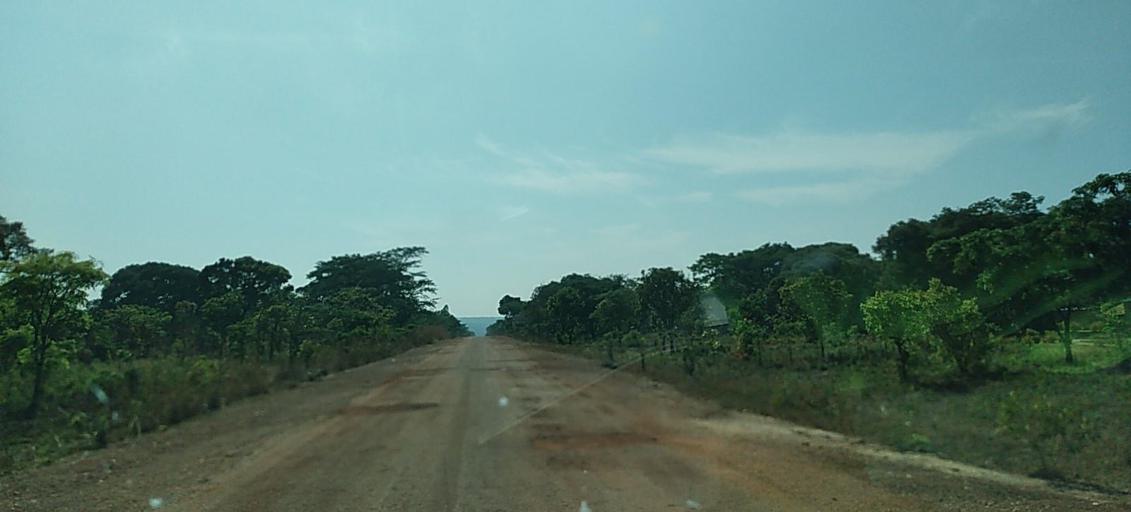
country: ZM
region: North-Western
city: Mwinilunga
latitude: -11.8217
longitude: 25.1012
